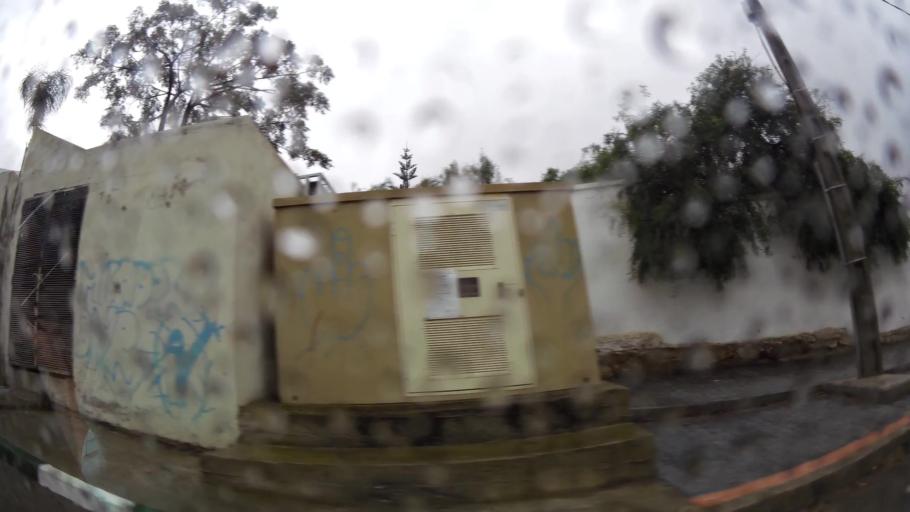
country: MA
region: Taza-Al Hoceima-Taounate
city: Al Hoceima
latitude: 35.2492
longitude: -3.9461
